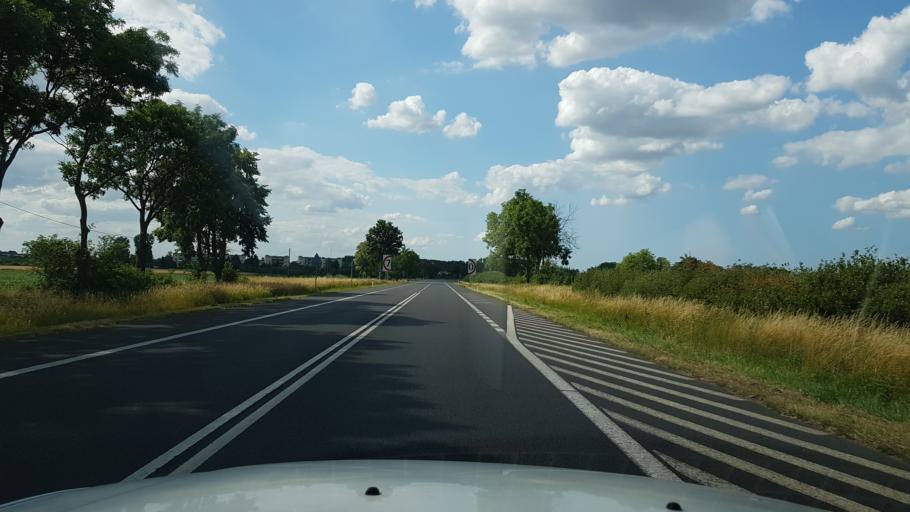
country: PL
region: West Pomeranian Voivodeship
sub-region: Powiat pyrzycki
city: Pyrzyce
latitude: 53.1767
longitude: 14.8479
